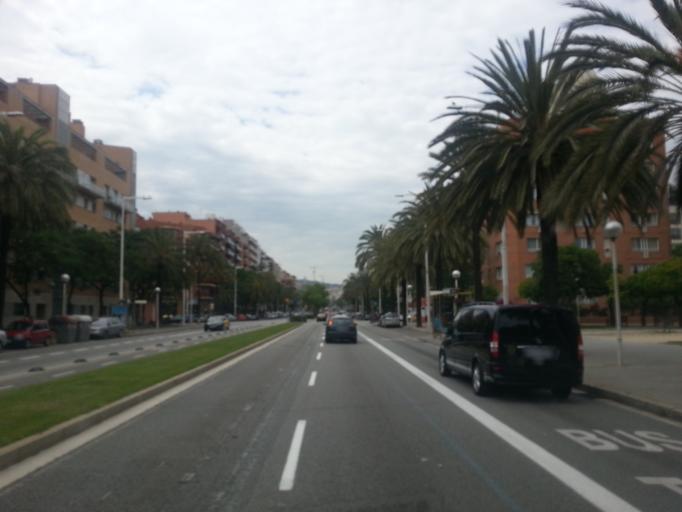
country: ES
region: Catalonia
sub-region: Provincia de Barcelona
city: Ciutat Vella
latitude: 41.3907
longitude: 2.1925
